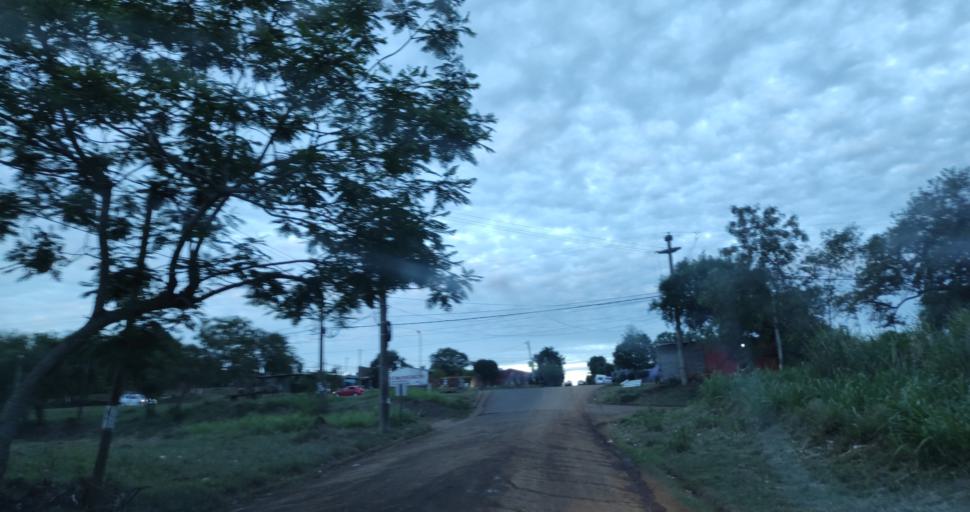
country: AR
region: Misiones
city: Garupa
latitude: -27.4717
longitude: -55.8454
